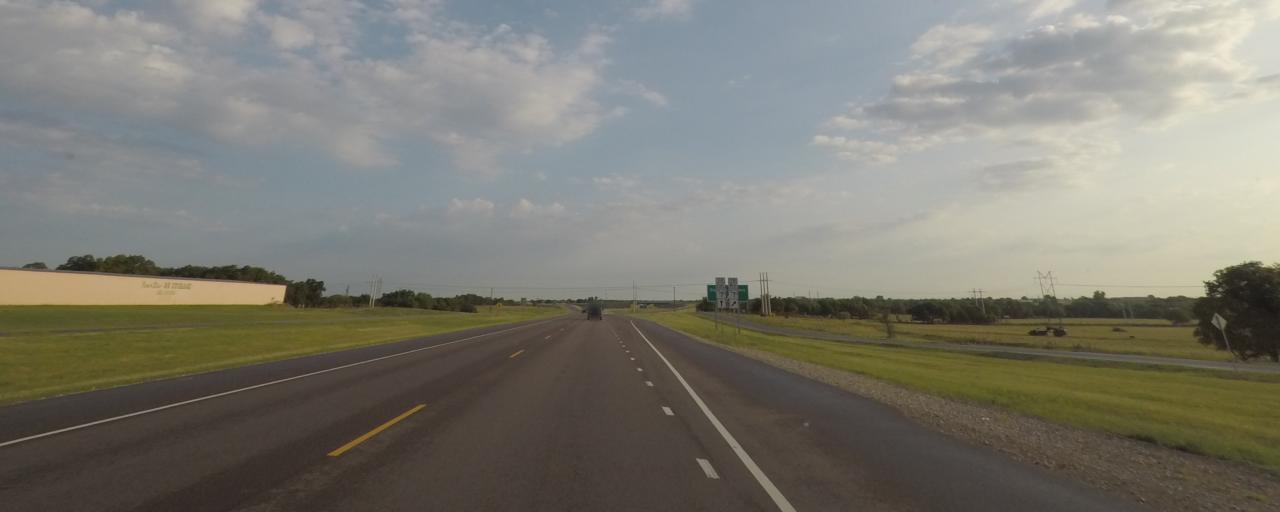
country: US
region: Oklahoma
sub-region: Stephens County
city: Meridian
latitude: 34.4603
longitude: -97.9741
